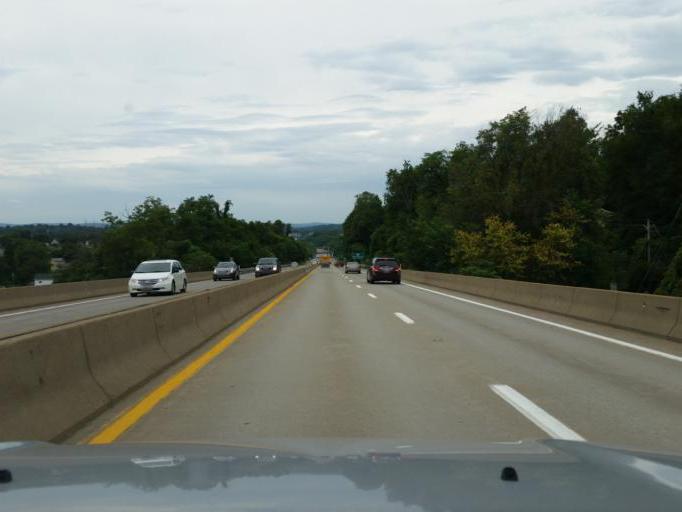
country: US
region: Pennsylvania
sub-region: Westmoreland County
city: Southwest Greensburg
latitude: 40.3038
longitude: -79.5632
